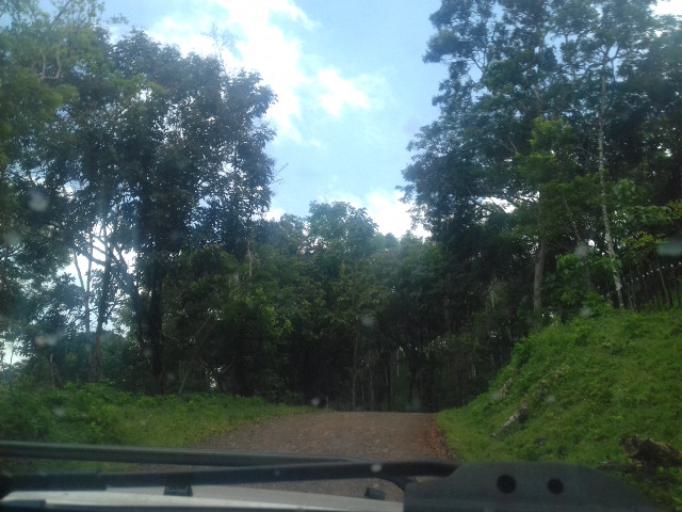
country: NI
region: Matagalpa
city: Matiguas
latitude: 12.9194
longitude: -85.3648
